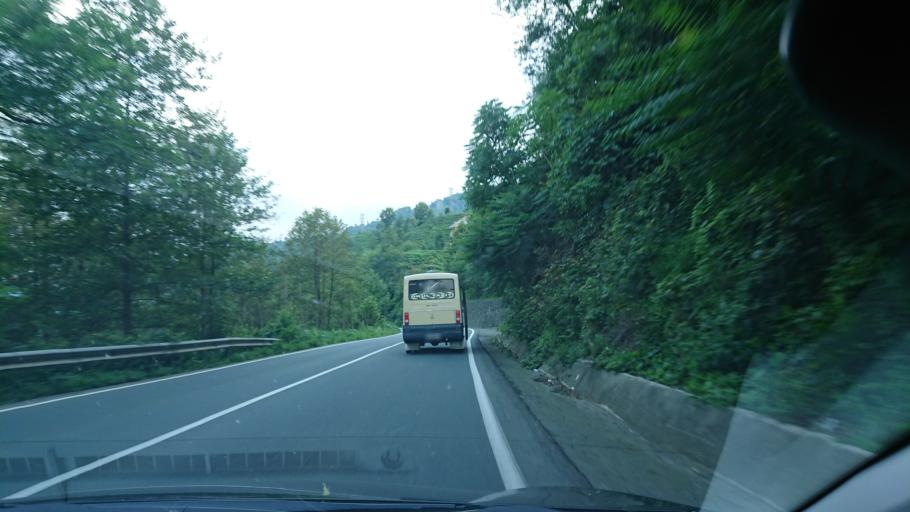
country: TR
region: Rize
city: Cayeli
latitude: 41.0740
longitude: 40.7114
